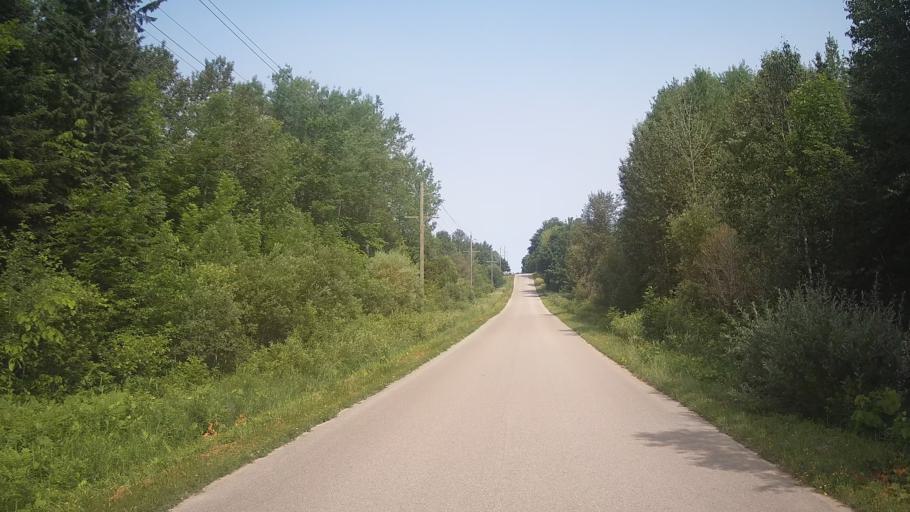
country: CA
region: Ontario
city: Barrie
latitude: 44.4508
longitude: -79.6263
